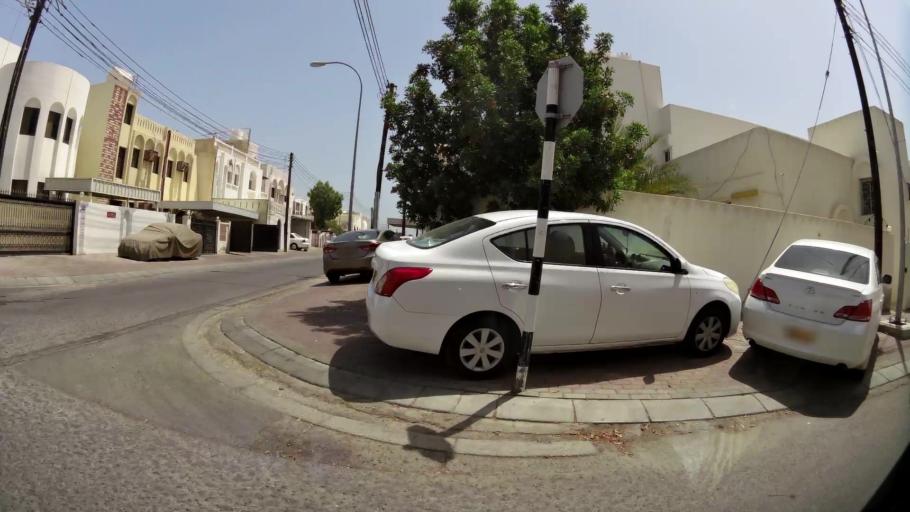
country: OM
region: Muhafazat Masqat
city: Bawshar
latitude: 23.5896
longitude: 58.4330
